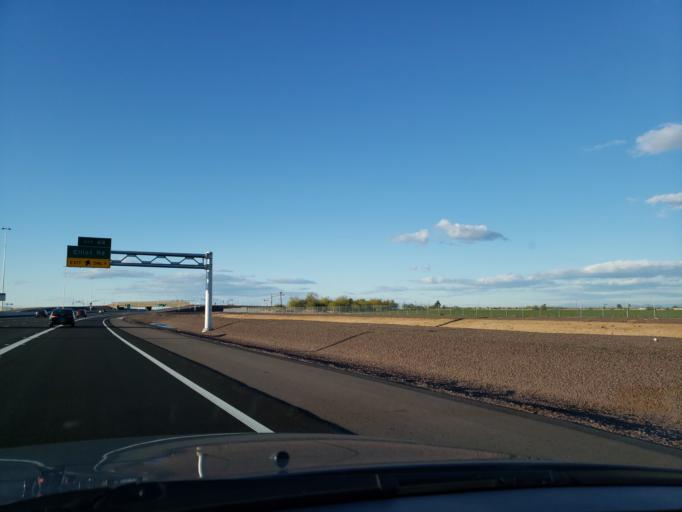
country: US
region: Arizona
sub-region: Maricopa County
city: Laveen
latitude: 33.3432
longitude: -112.1859
